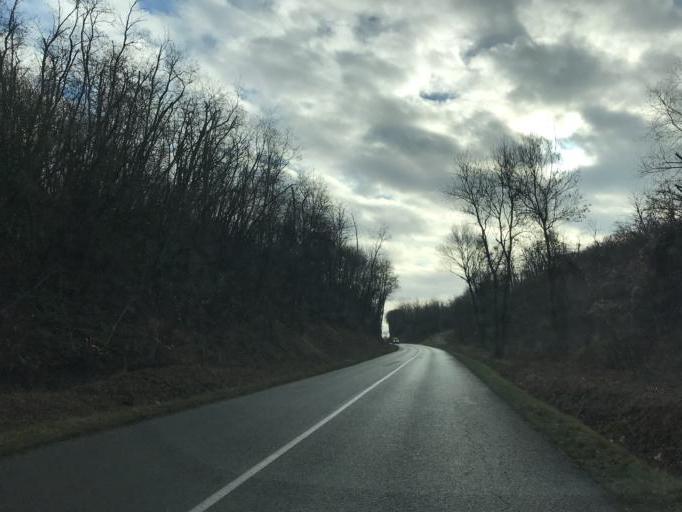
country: FR
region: Rhone-Alpes
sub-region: Departement de l'Ain
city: Sainte-Euphemie
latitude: 45.9645
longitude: 4.7985
